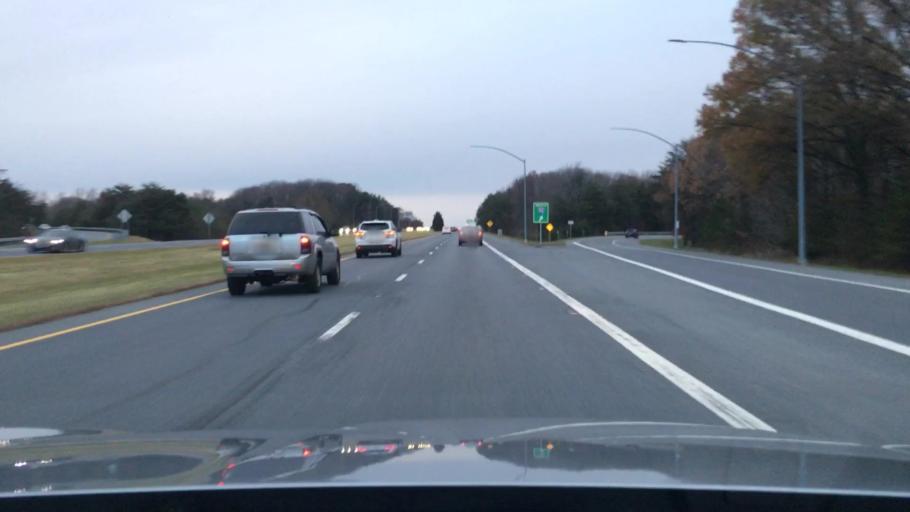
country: US
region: Maryland
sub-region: Howard County
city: North Laurel
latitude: 39.1249
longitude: -76.8578
